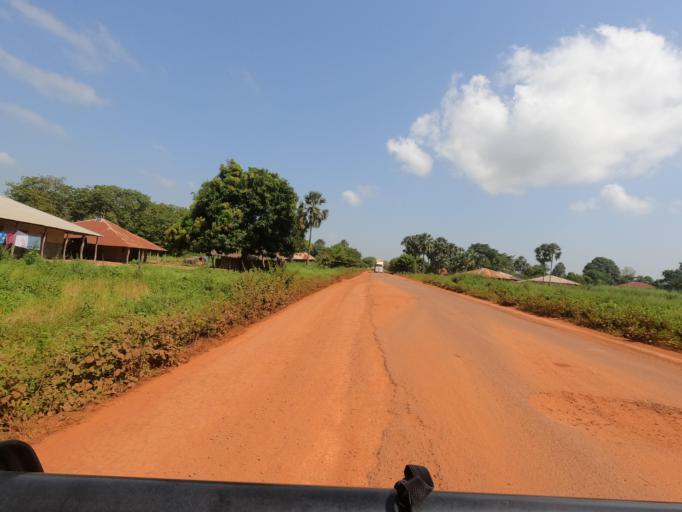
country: GW
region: Cacheu
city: Canchungo
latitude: 12.2812
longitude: -15.7851
